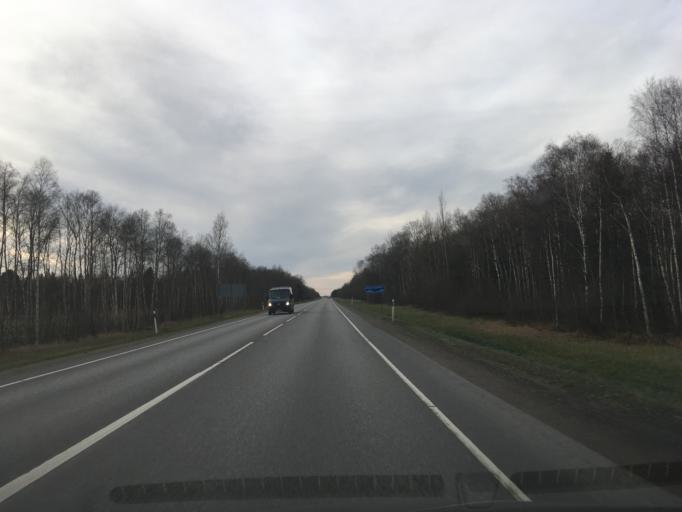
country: EE
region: Ida-Virumaa
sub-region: Kohtla-Jaerve linn
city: Kohtla-Jarve
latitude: 59.4207
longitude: 27.2693
